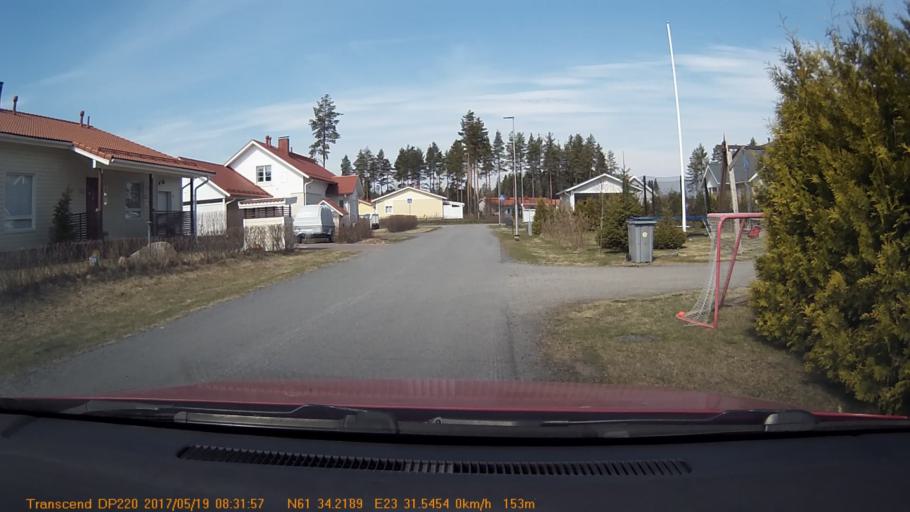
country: FI
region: Pirkanmaa
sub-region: Tampere
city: Yloejaervi
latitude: 61.5702
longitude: 23.5257
